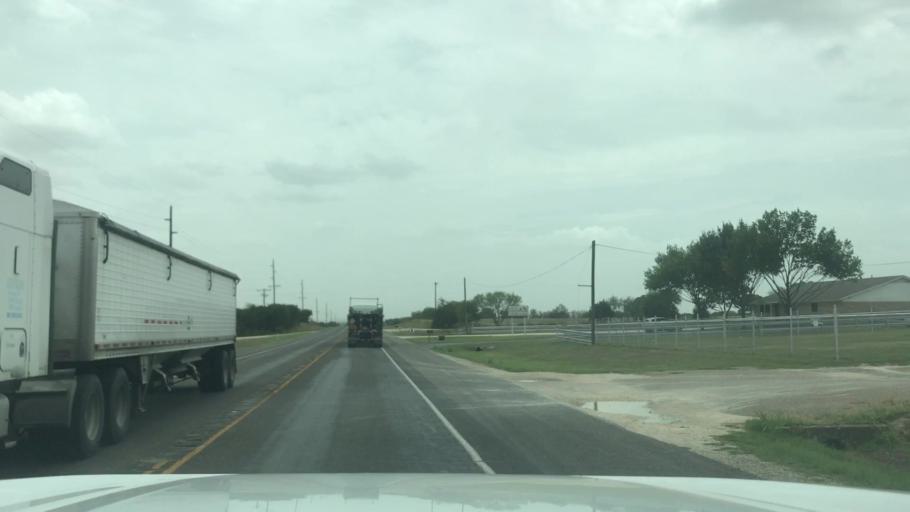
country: US
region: Texas
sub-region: Bosque County
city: Clifton
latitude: 31.7583
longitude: -97.5617
